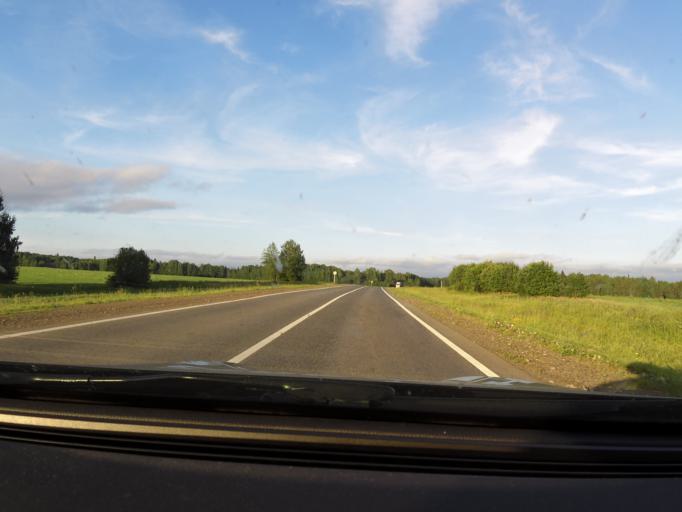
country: RU
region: Perm
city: Siva
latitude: 58.4897
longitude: 54.1148
